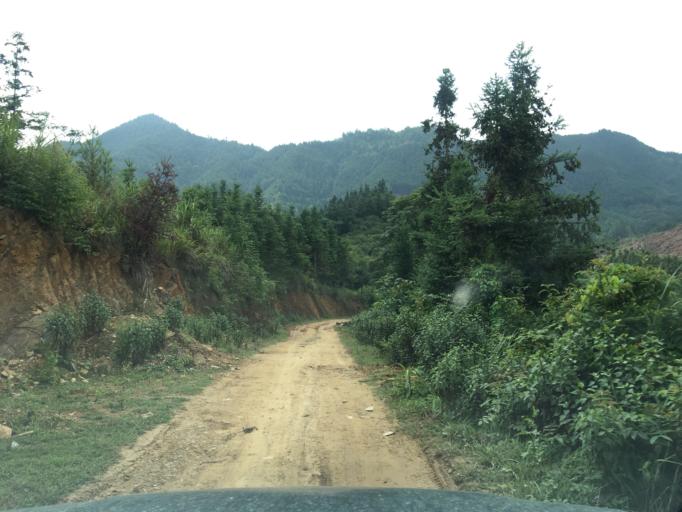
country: CN
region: Guangxi Zhuangzu Zizhiqu
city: Xinzhou
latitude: 24.8852
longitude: 105.8428
